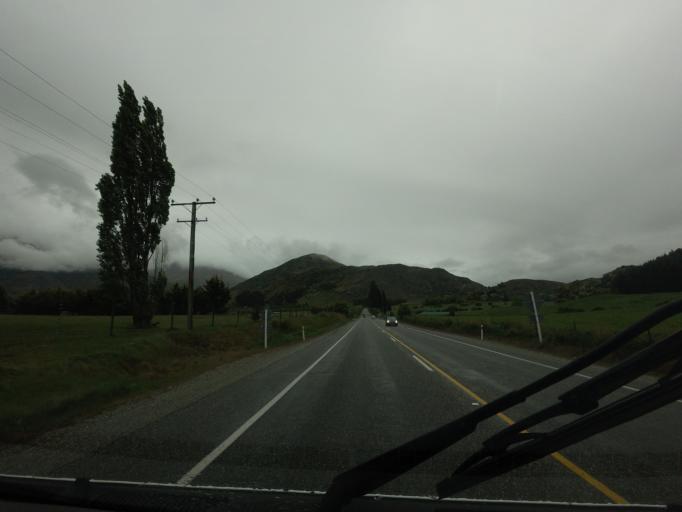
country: NZ
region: Otago
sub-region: Queenstown-Lakes District
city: Arrowtown
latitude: -44.9789
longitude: 168.8465
